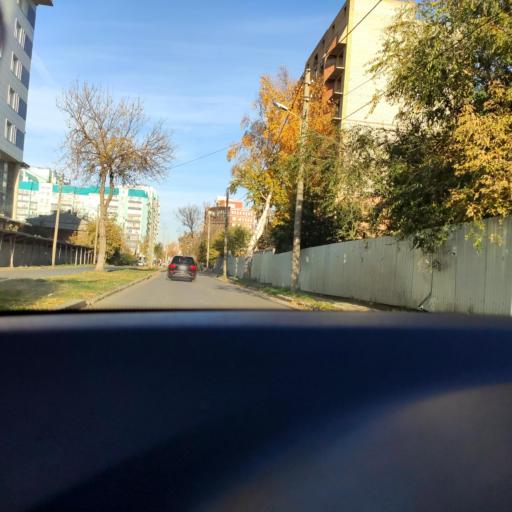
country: RU
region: Samara
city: Samara
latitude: 53.2003
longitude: 50.1195
